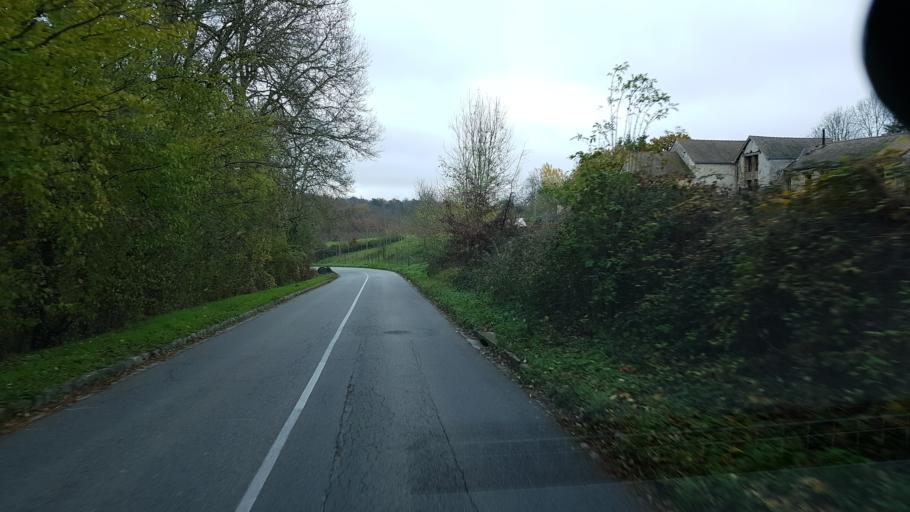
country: FR
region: Ile-de-France
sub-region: Departement des Yvelines
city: Chevreuse
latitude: 48.7176
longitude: 2.0154
